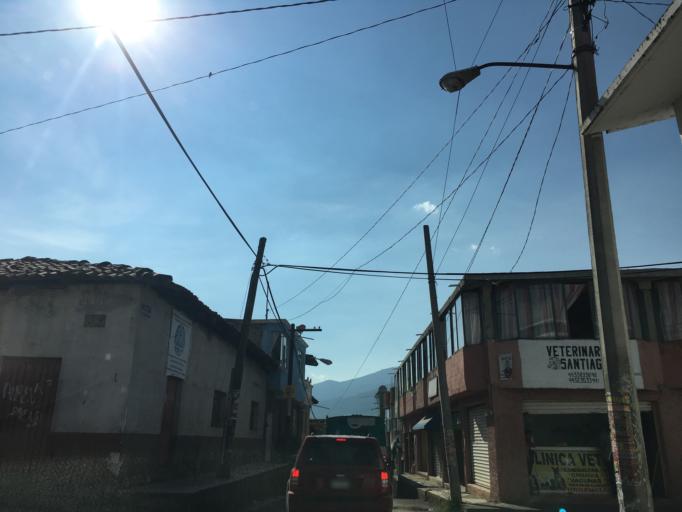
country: MX
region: Michoacan
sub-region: Morelia
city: La Mintzita (Piedra Dura)
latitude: 19.5951
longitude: -101.2852
